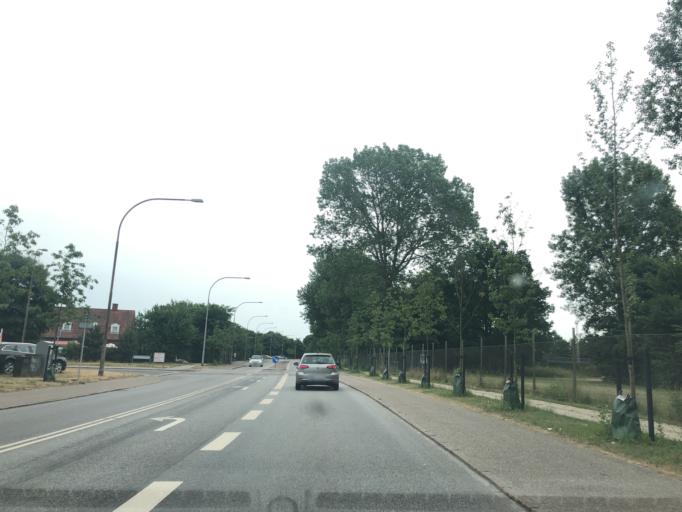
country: DK
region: Zealand
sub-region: Koge Kommune
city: Koge
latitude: 55.4700
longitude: 12.1736
